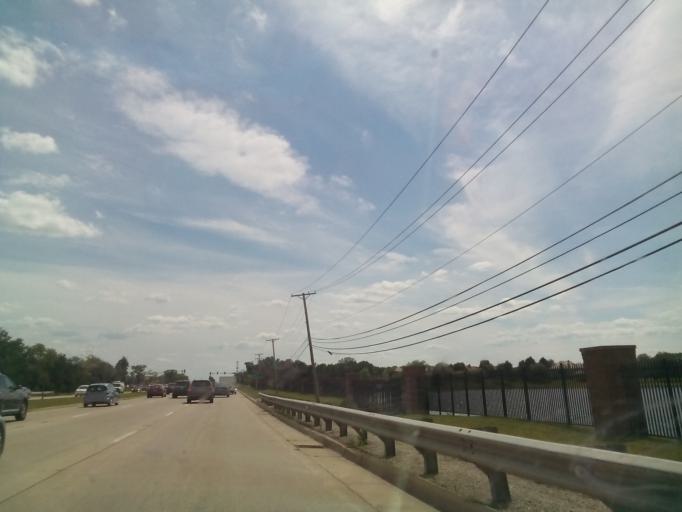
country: US
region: Illinois
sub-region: DuPage County
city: Naperville
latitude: 41.7294
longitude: -88.2063
